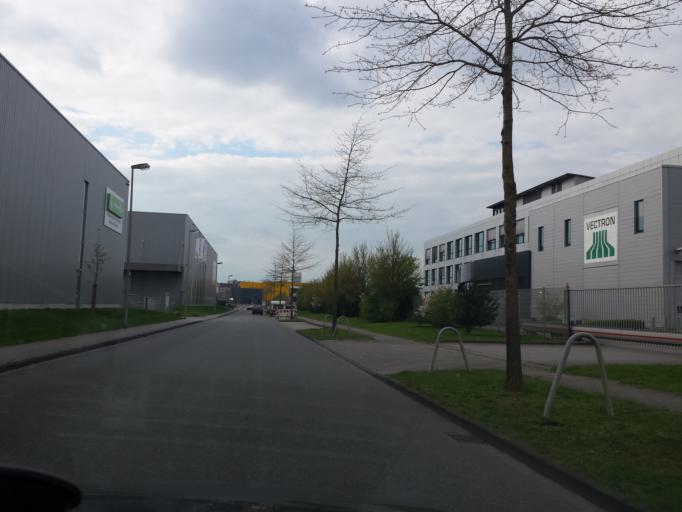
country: DE
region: North Rhine-Westphalia
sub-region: Regierungsbezirk Munster
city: Muenster
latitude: 51.9332
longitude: 7.6474
